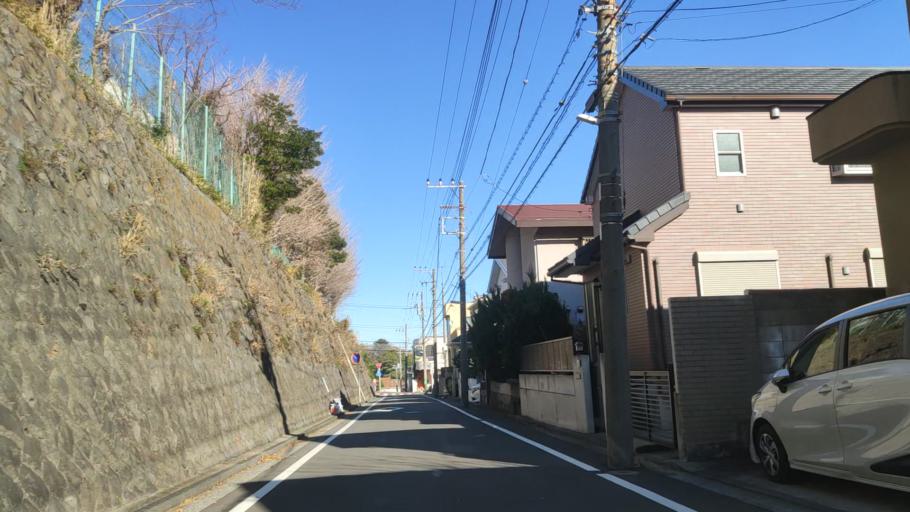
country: JP
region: Kanagawa
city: Yokohama
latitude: 35.4240
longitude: 139.6534
